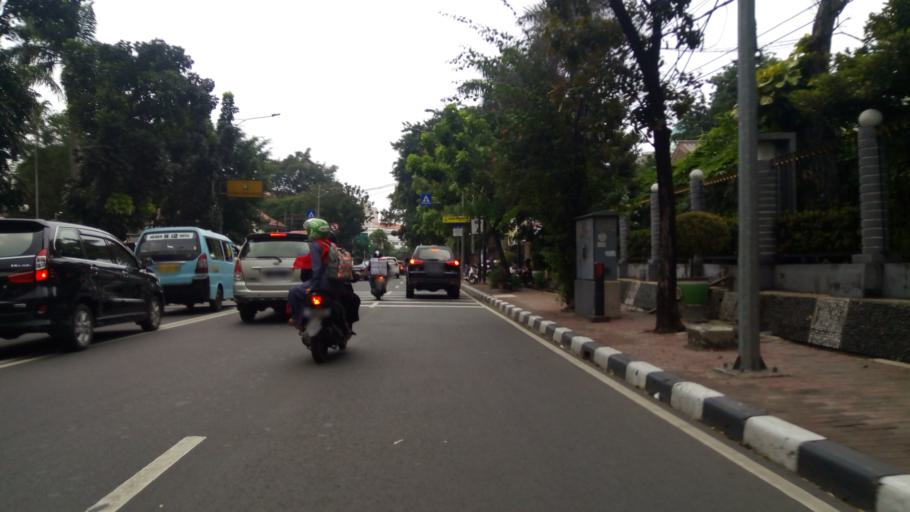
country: ID
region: Jakarta Raya
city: Jakarta
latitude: -6.1705
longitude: 106.8385
